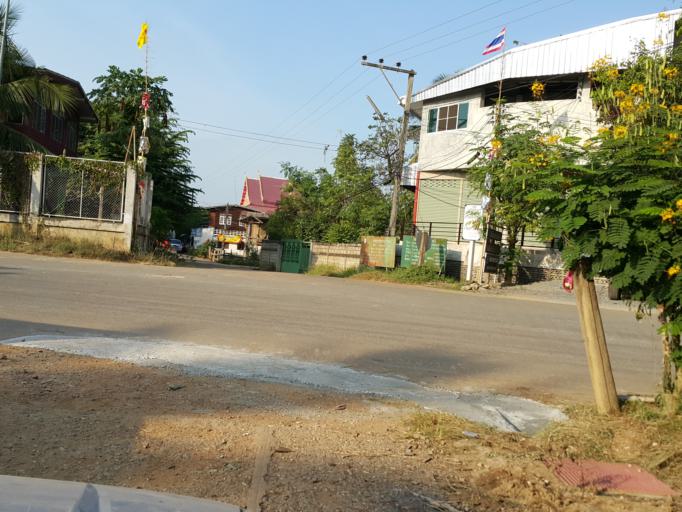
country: TH
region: Sukhothai
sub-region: Amphoe Si Satchanalai
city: Si Satchanalai
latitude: 17.4717
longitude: 99.6475
